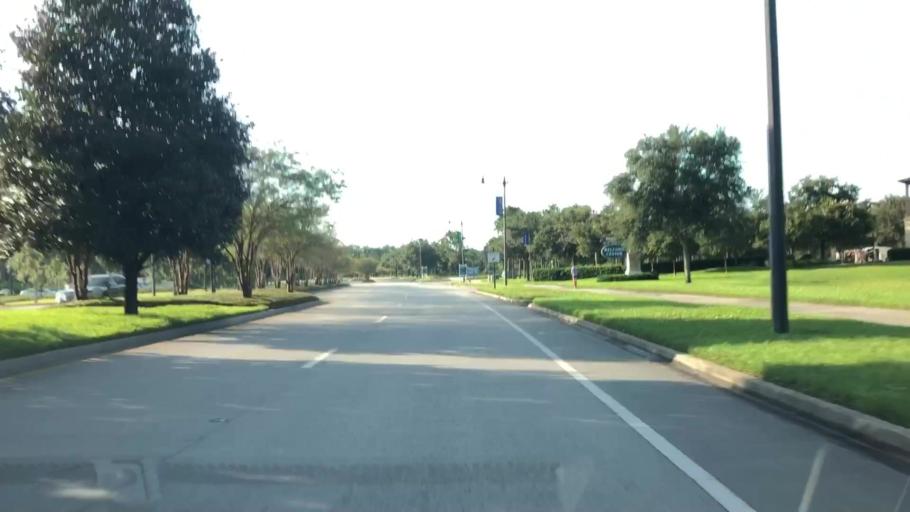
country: US
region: Florida
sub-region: Saint Johns County
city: Palm Valley
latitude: 30.1042
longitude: -81.4150
